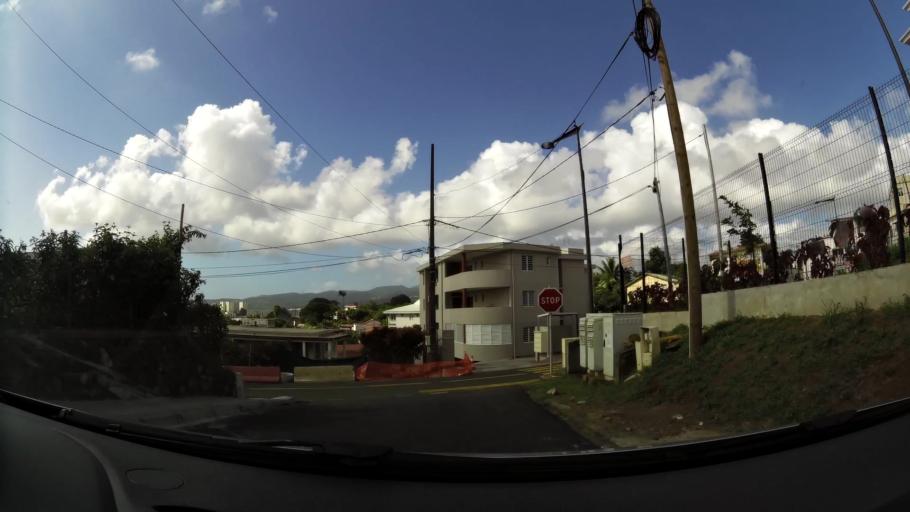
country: MQ
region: Martinique
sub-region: Martinique
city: Fort-de-France
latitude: 14.6268
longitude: -61.0593
